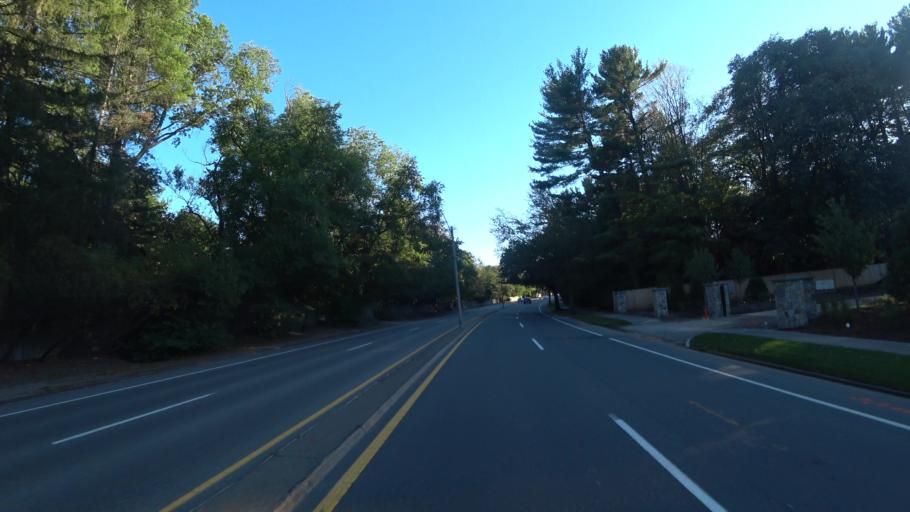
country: US
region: Massachusetts
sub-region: Suffolk County
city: Jamaica Plain
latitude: 42.3181
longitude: -71.1409
